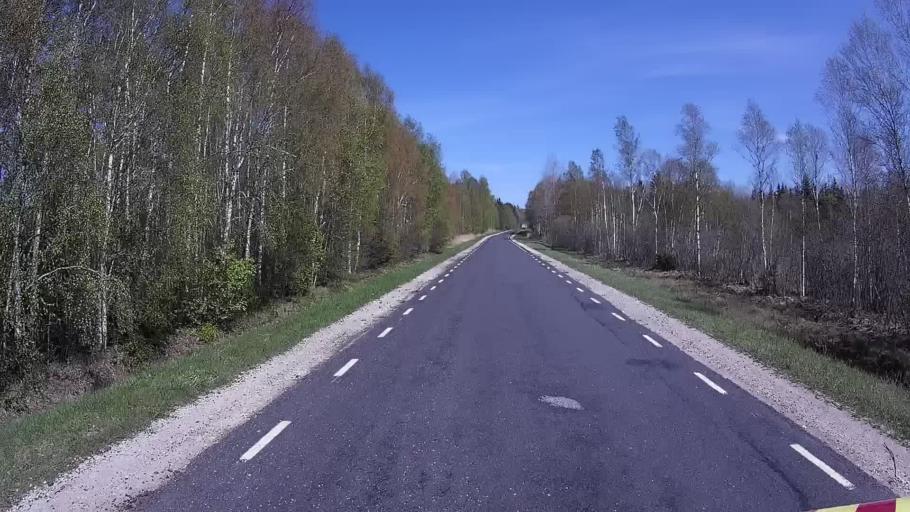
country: EE
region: Laeaene
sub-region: Ridala Parish
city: Uuemoisa
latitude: 59.0229
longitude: 23.8038
